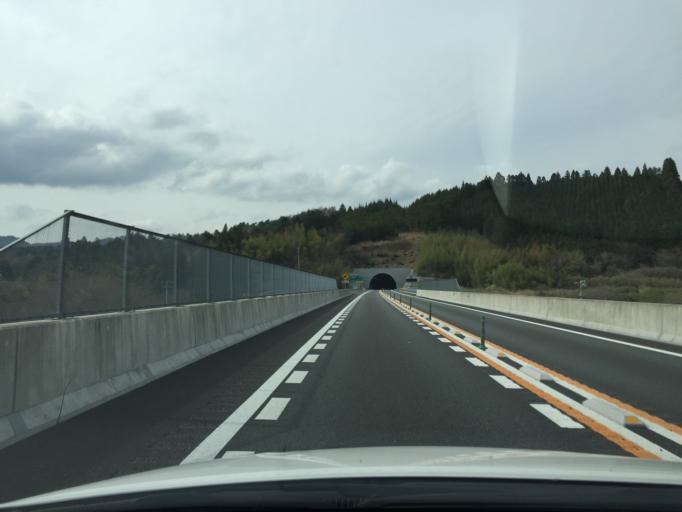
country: JP
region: Fukushima
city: Namie
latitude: 37.5865
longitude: 140.9324
